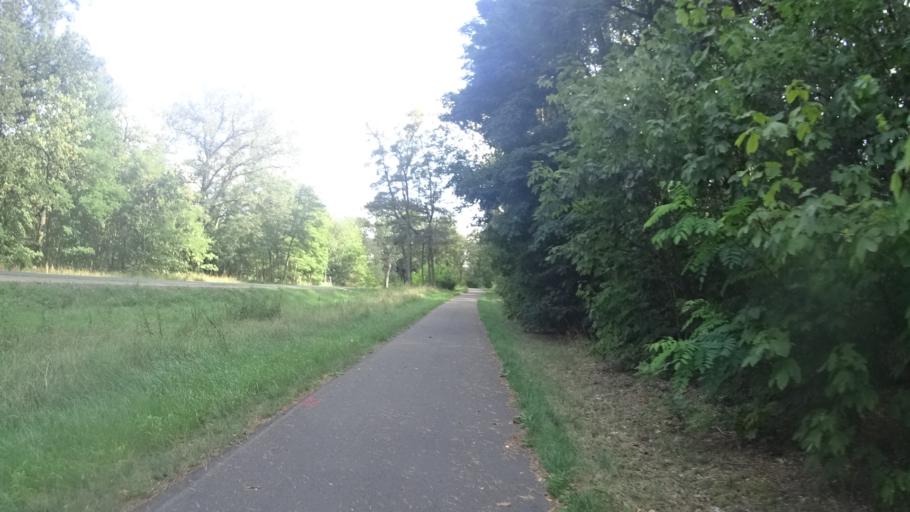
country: DE
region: Brandenburg
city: Rhinow
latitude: 52.7165
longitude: 12.3661
